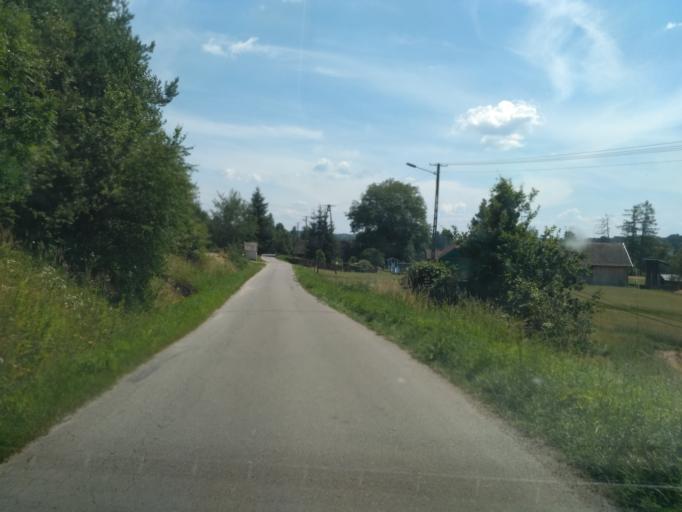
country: PL
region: Subcarpathian Voivodeship
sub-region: Powiat strzyzowski
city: Strzyzow
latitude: 49.8531
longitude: 21.8043
